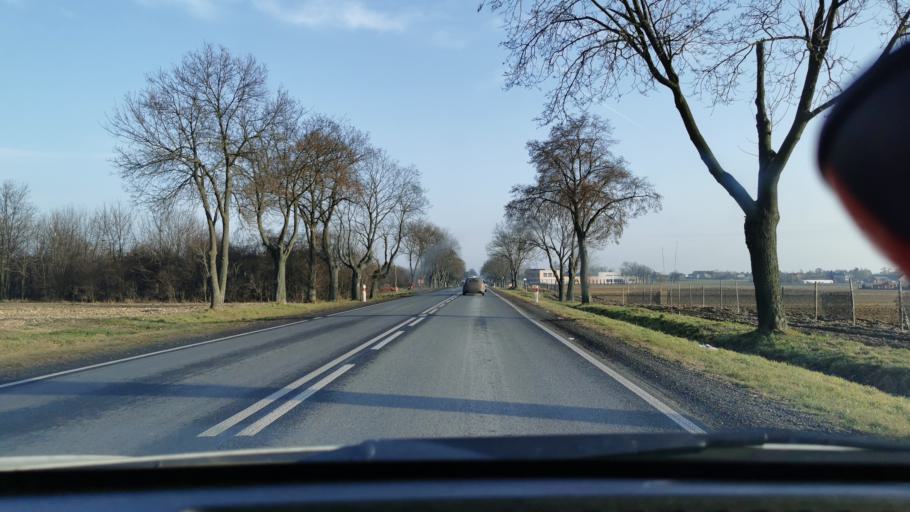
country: PL
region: Lodz Voivodeship
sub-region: Powiat sieradzki
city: Wroblew
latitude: 51.6335
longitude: 18.5396
